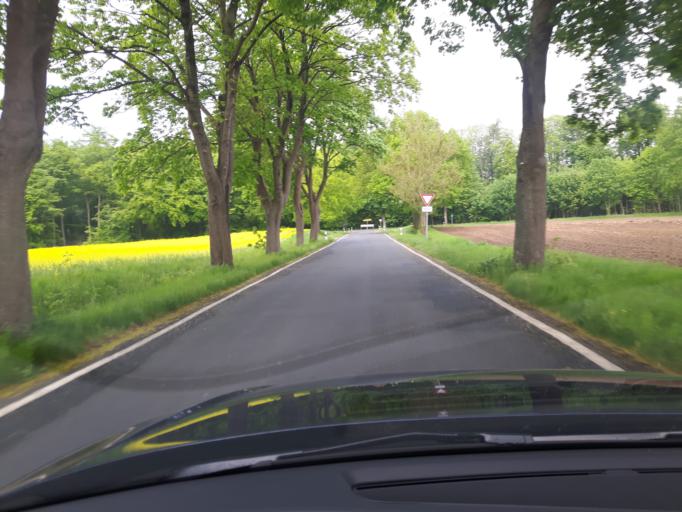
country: DE
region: Mecklenburg-Vorpommern
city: Velgast
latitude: 54.2280
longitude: 12.7322
